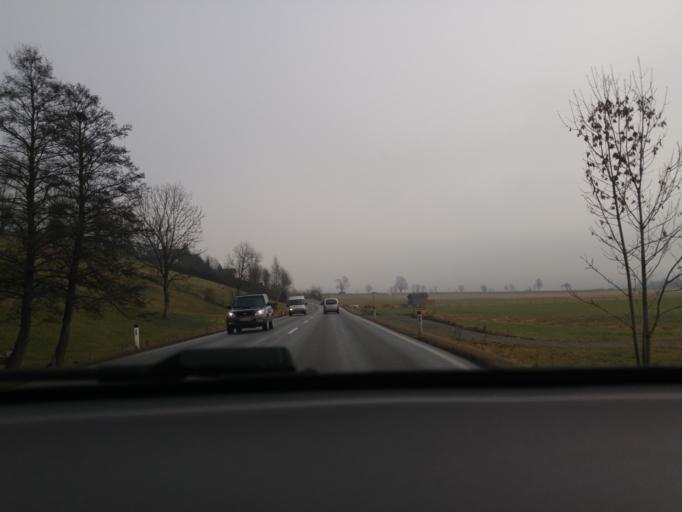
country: AT
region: Salzburg
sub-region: Politischer Bezirk Zell am See
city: Niedernsill
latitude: 47.2858
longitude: 12.6787
